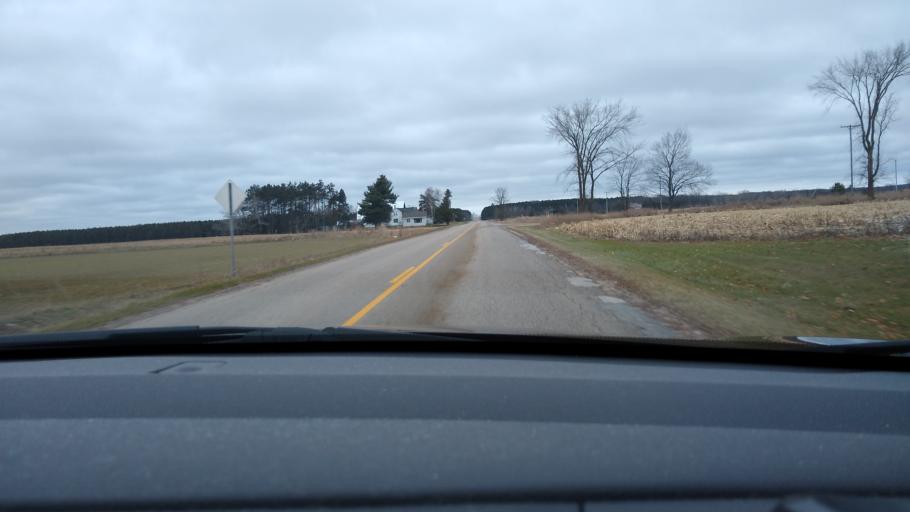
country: US
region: Michigan
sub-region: Missaukee County
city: Lake City
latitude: 44.2496
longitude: -85.0536
